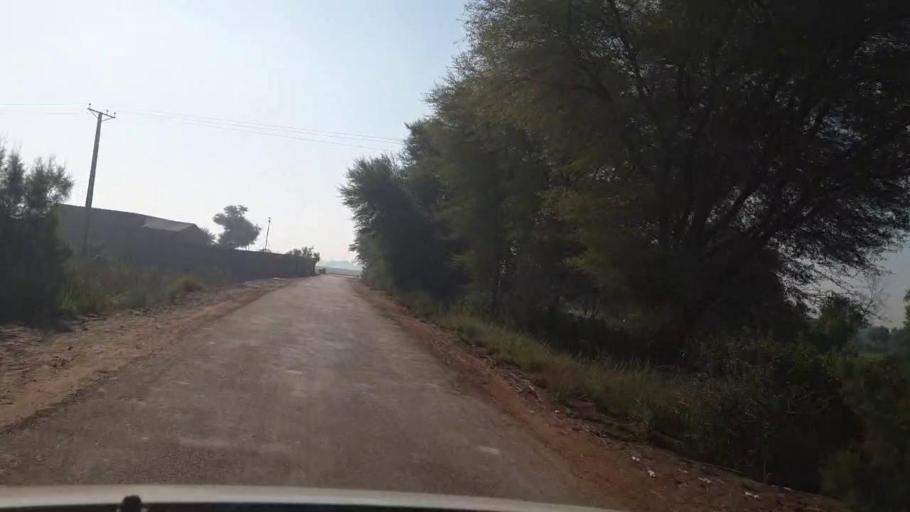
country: PK
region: Sindh
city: Dadu
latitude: 26.6558
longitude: 67.8224
